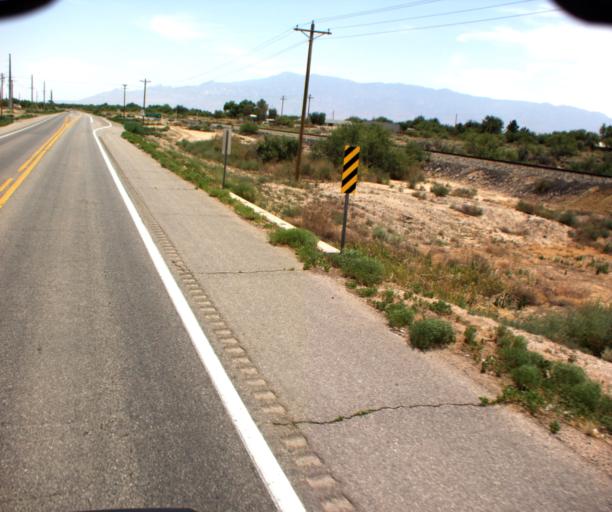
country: US
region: Arizona
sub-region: Graham County
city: Pima
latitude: 32.9492
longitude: -109.9128
